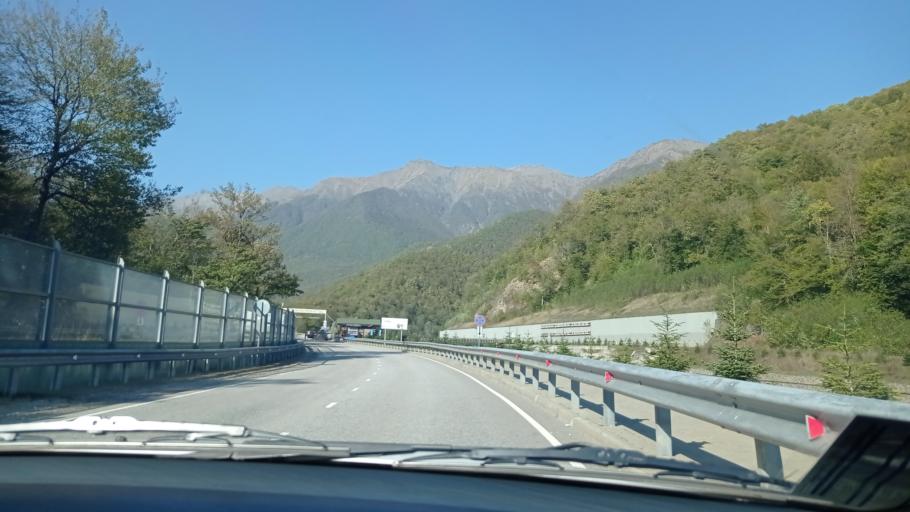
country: RU
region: Krasnodarskiy
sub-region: Sochi City
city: Krasnaya Polyana
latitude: 43.6960
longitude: 40.2693
